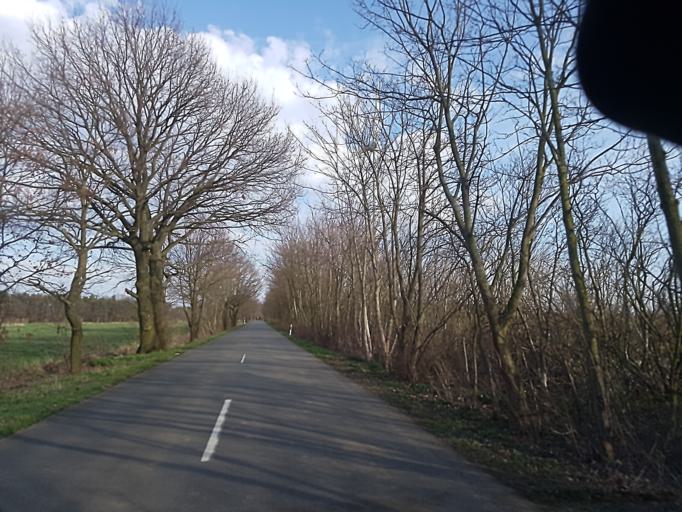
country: DE
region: Brandenburg
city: Falkenberg
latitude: 51.5444
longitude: 13.3091
